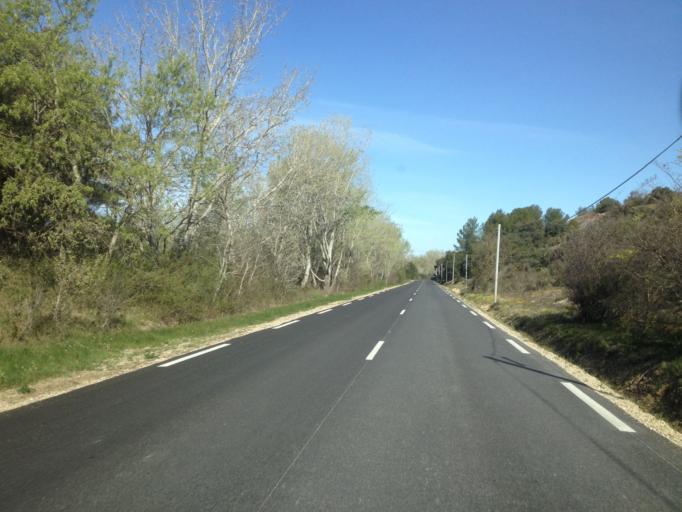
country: FR
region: Languedoc-Roussillon
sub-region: Departement du Gard
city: Roquemaure
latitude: 44.0693
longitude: 4.7884
